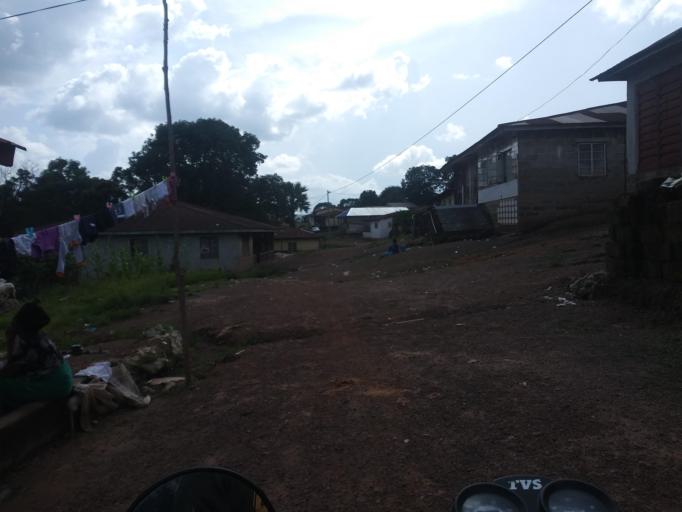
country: SL
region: Northern Province
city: Makeni
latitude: 8.8902
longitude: -12.0350
